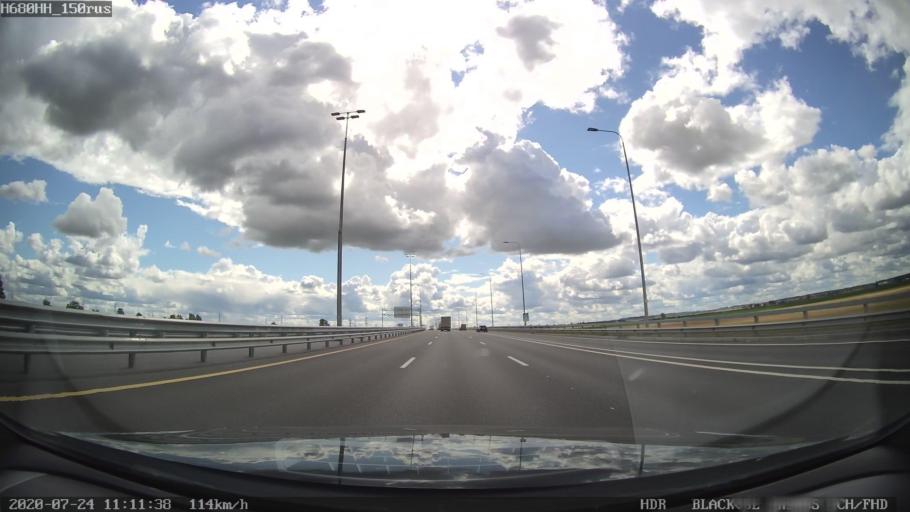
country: RU
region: Leningrad
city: Fedorovskoye
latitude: 59.7201
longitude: 30.5188
